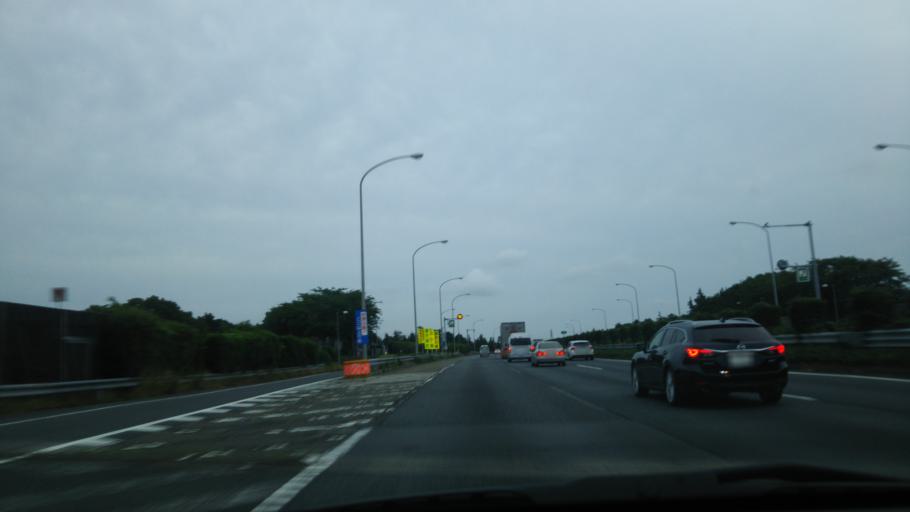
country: JP
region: Kanagawa
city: Minami-rinkan
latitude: 35.4788
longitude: 139.4530
